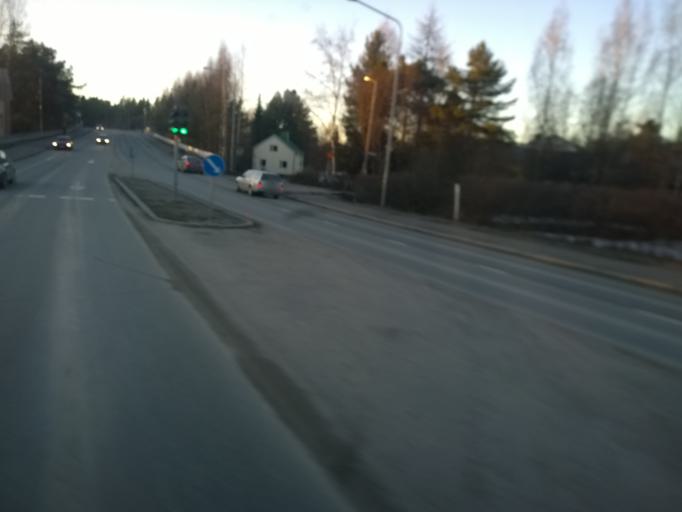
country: FI
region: Pirkanmaa
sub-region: Tampere
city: Tampere
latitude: 61.4871
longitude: 23.8234
